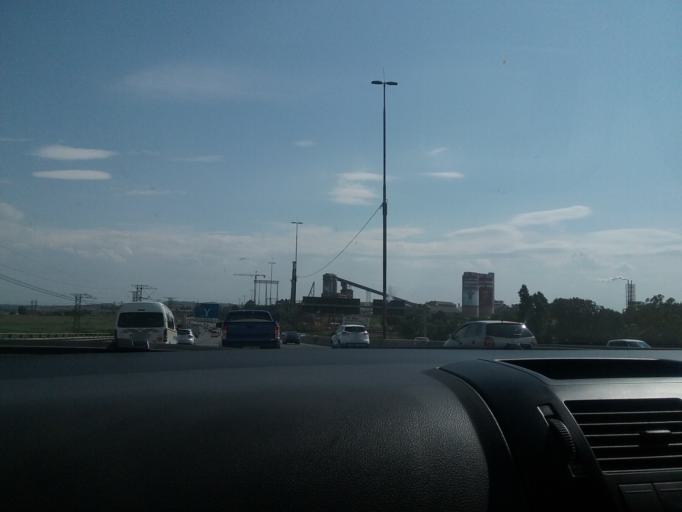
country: ZA
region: Gauteng
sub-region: Ekurhuleni Metropolitan Municipality
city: Germiston
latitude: -26.2180
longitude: 28.1305
